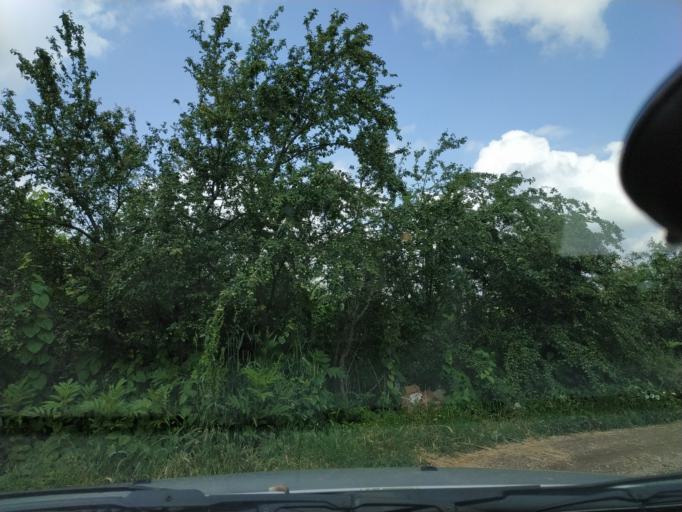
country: RS
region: Central Serbia
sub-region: Nisavski Okrug
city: Aleksinac
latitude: 43.4249
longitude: 21.5843
